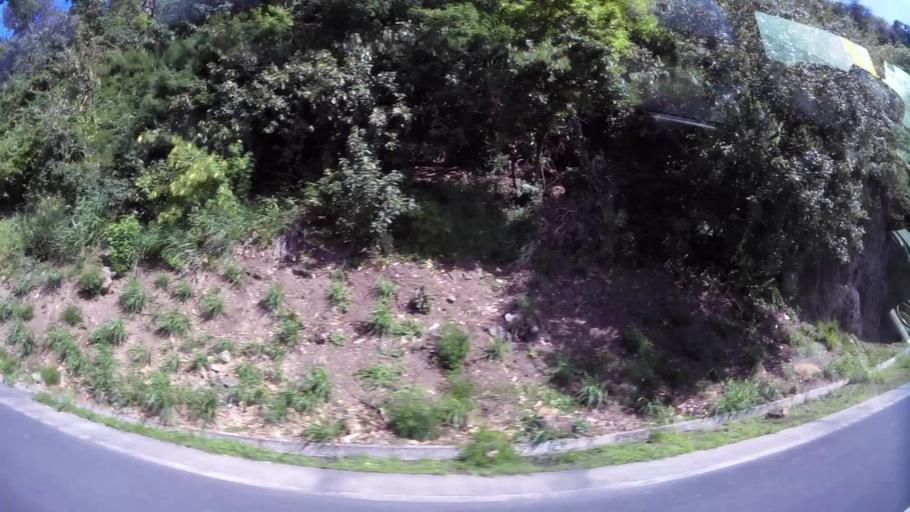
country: DM
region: Saint George
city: Roseau
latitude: 15.3199
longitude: -61.3936
